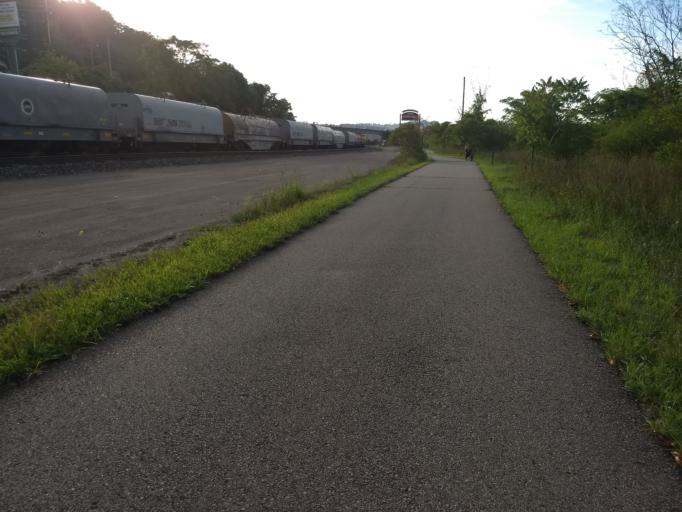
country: US
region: Pennsylvania
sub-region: Allegheny County
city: Whitaker
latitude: 40.4066
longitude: -79.8865
